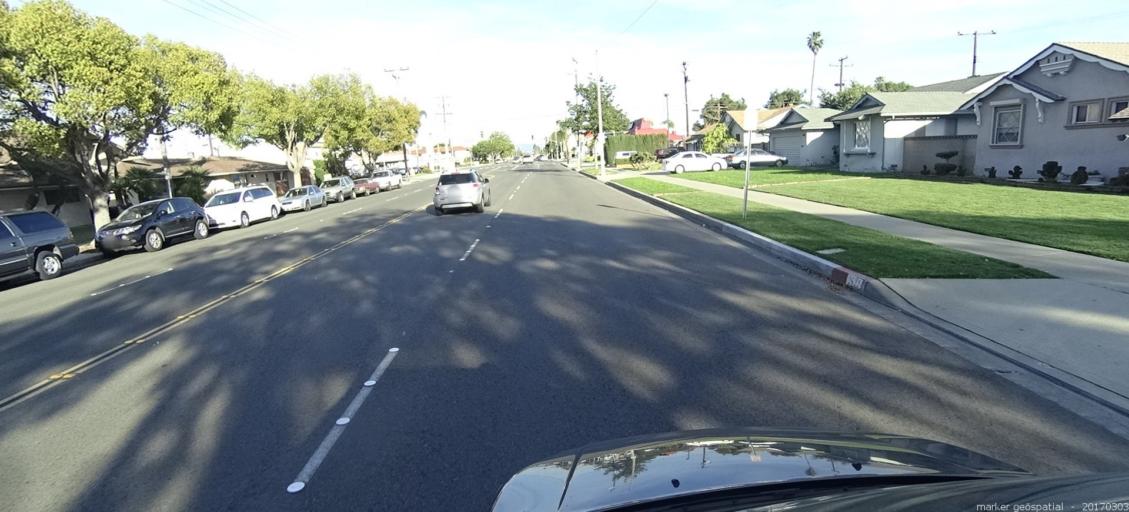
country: US
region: California
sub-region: Orange County
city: Stanton
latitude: 33.8285
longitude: -117.9775
